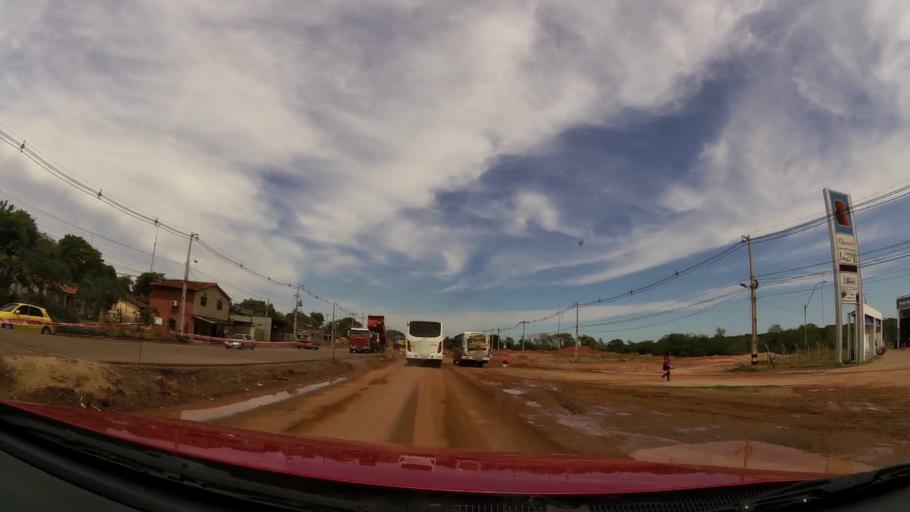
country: PY
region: Central
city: Limpio
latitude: -25.1924
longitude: -57.5059
